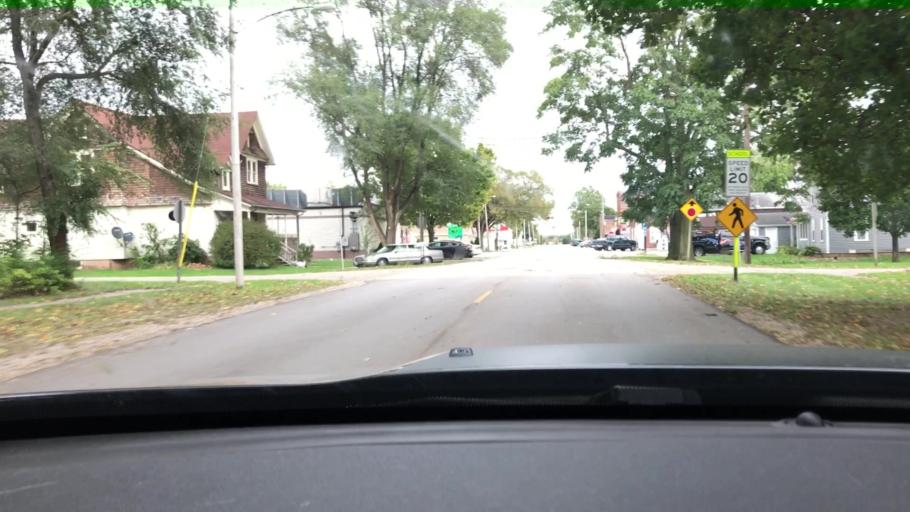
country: US
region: Illinois
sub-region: LaSalle County
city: Sheridan
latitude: 41.5299
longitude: -88.6826
